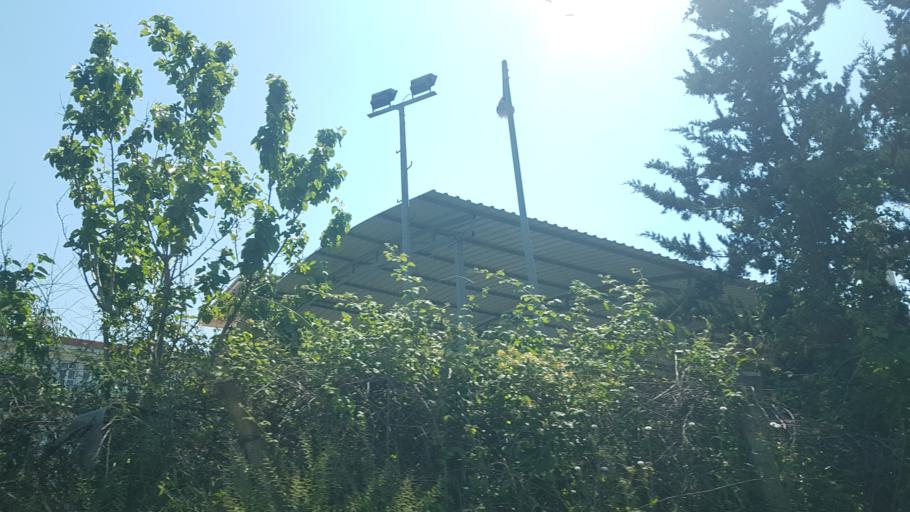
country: TR
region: Adana
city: Adana
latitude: 37.0294
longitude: 35.3577
